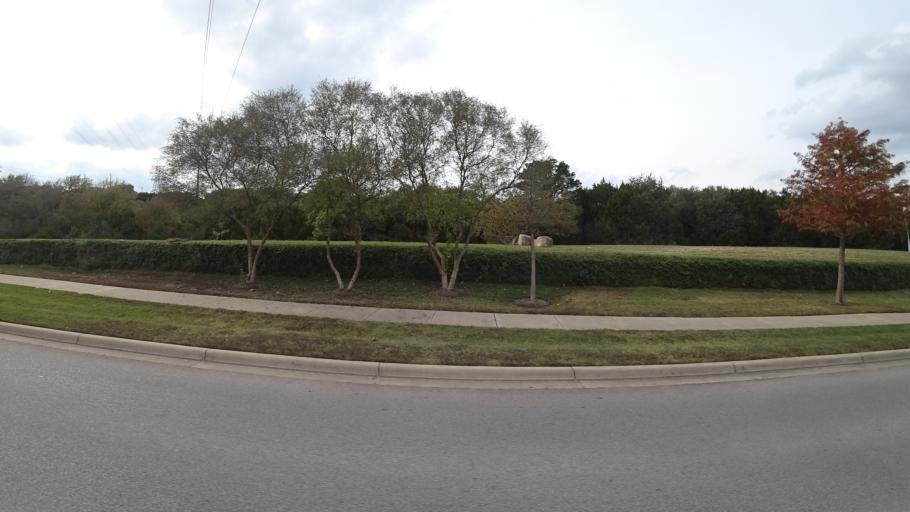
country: US
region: Texas
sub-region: Travis County
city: Hudson Bend
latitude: 30.3848
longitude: -97.8831
